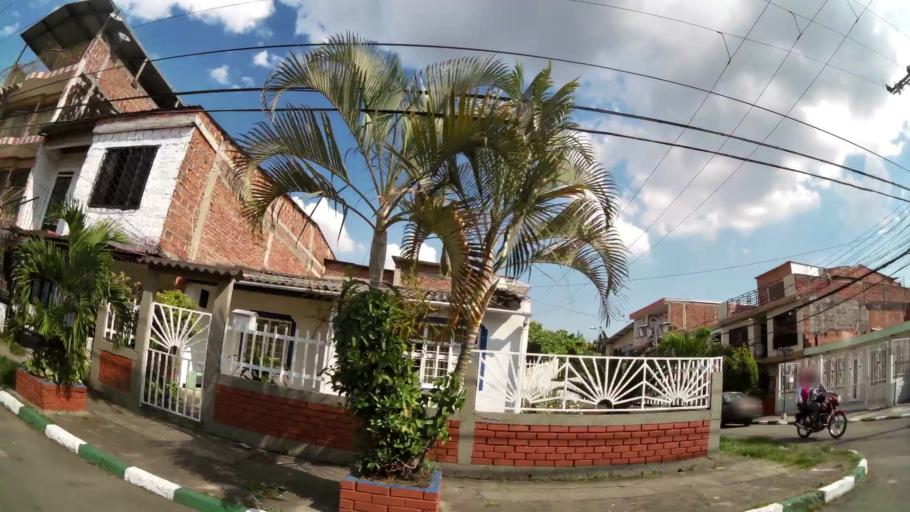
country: CO
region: Valle del Cauca
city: Cali
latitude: 3.4169
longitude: -76.5118
